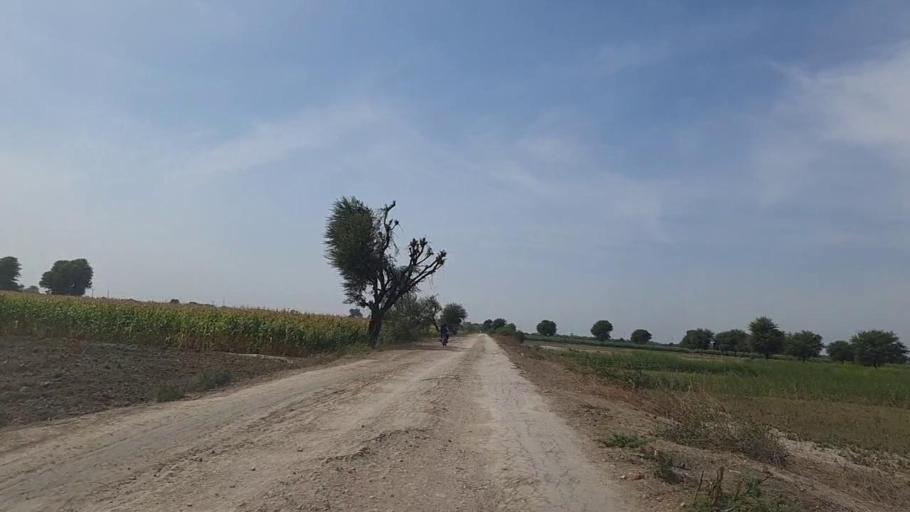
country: PK
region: Sindh
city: Samaro
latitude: 25.2129
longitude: 69.4663
